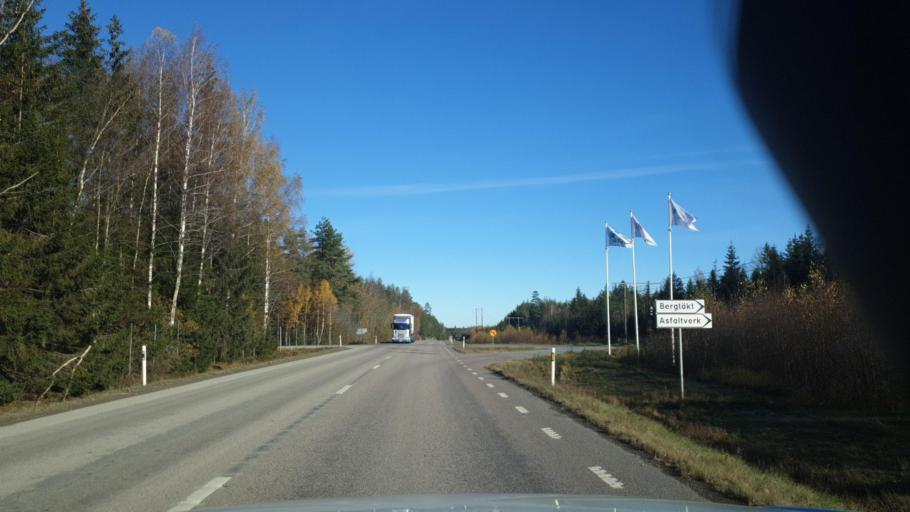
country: SE
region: Vaermland
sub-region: Karlstads Kommun
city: Edsvalla
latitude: 59.4173
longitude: 13.1871
